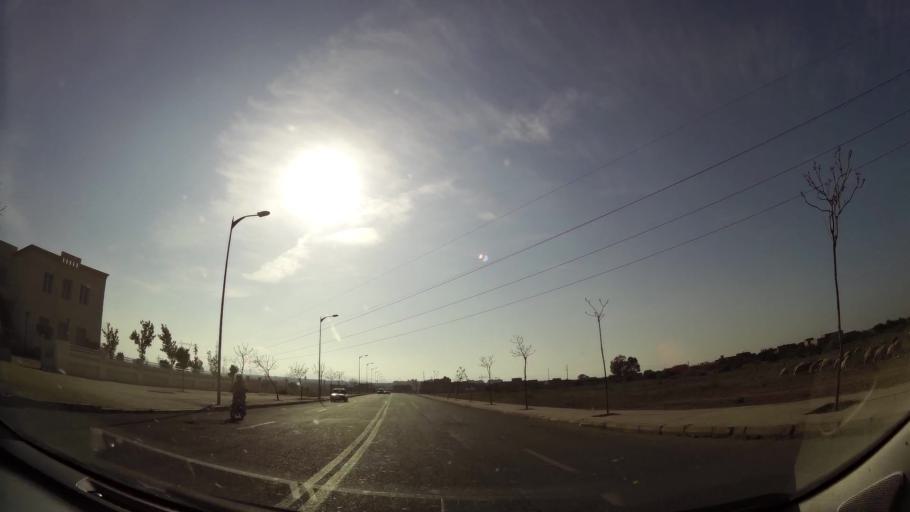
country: MA
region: Oriental
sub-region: Oujda-Angad
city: Oujda
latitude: 34.7197
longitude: -1.9006
